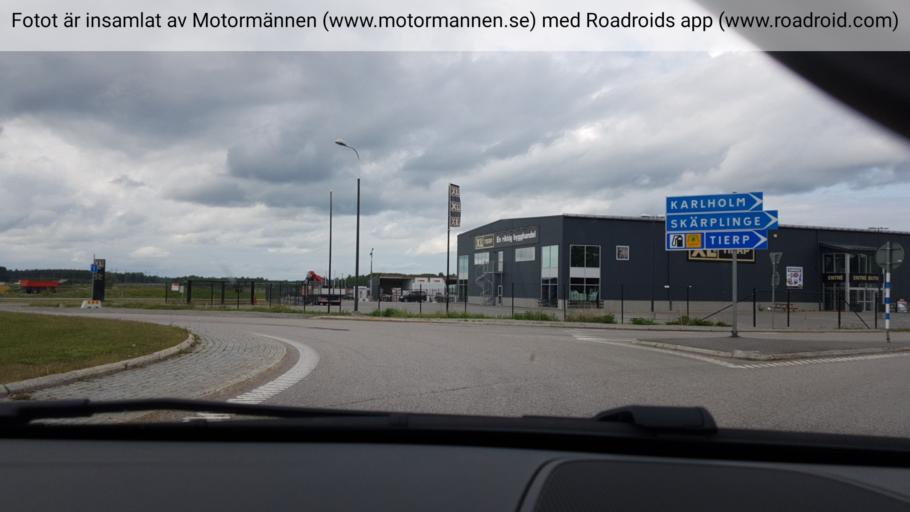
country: SE
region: Uppsala
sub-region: Tierps Kommun
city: Tierp
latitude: 60.3457
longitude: 17.4915
